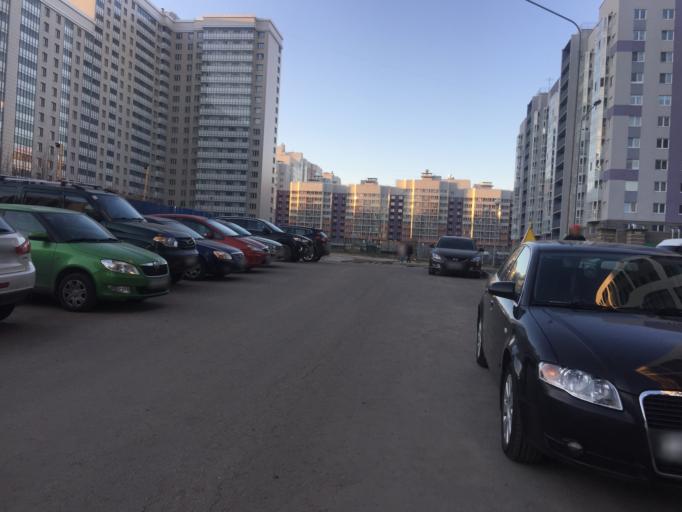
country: RU
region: Leningrad
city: Murino
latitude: 60.0546
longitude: 30.4357
